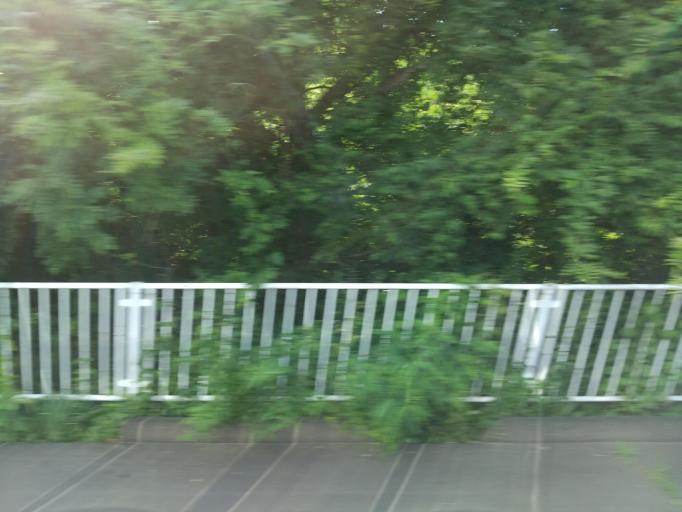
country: JP
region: Miyagi
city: Sendai
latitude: 38.2550
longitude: 140.7549
